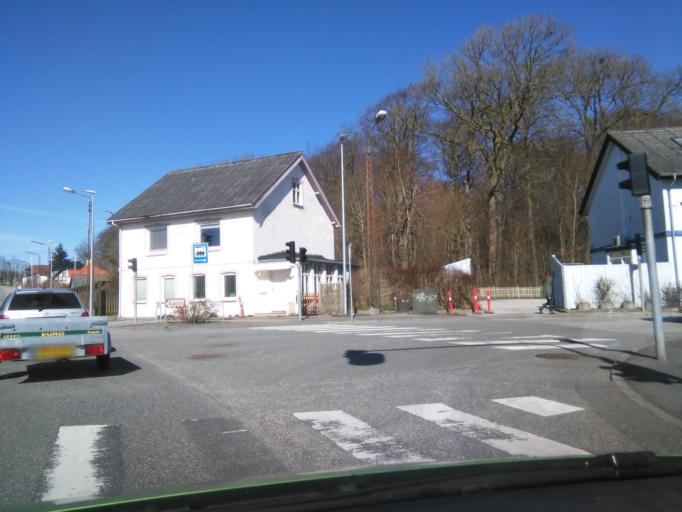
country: DK
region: Central Jutland
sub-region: Arhus Kommune
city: Lystrup
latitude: 56.2318
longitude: 10.2314
